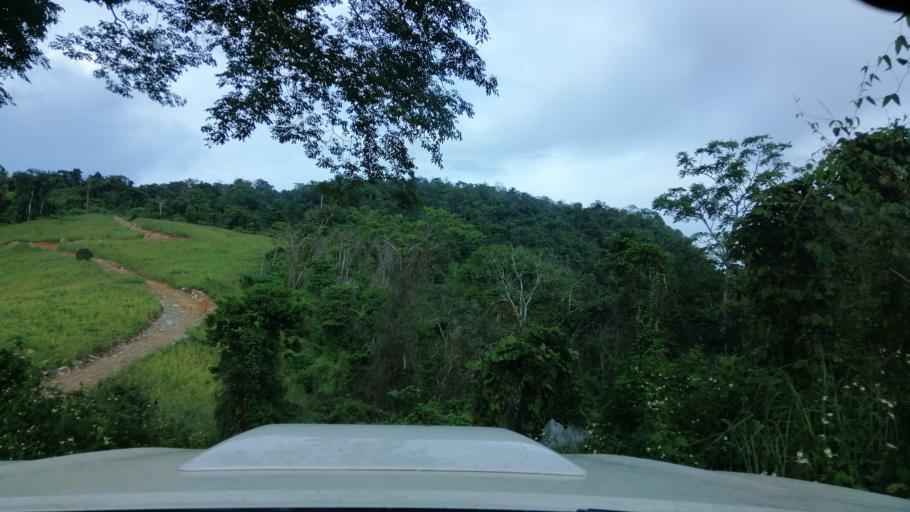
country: TH
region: Nan
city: Chaloem Phra Kiat
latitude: 19.7581
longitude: 101.1129
